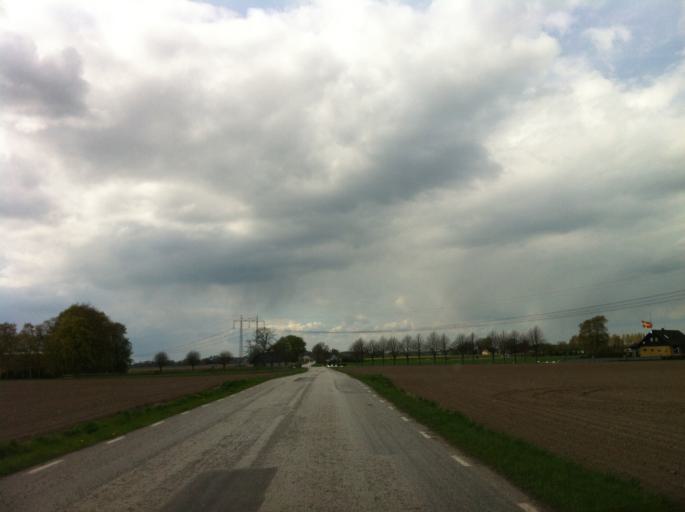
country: SE
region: Skane
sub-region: Kavlinge Kommun
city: Kaevlinge
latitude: 55.8153
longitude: 13.1356
